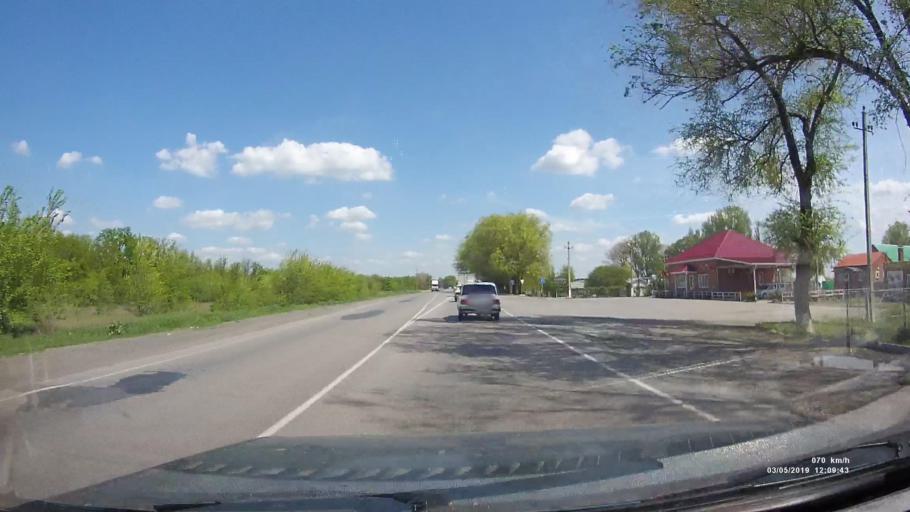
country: RU
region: Rostov
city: Bagayevskaya
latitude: 47.2962
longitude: 40.5201
